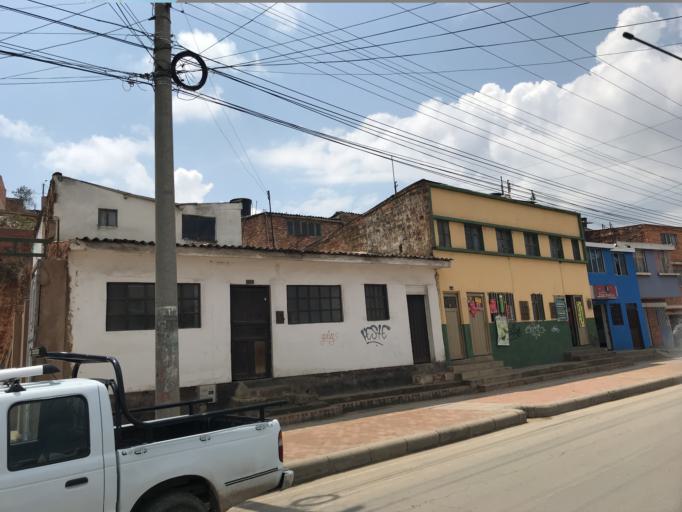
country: CO
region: Boyaca
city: Tunja
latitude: 5.5405
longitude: -73.3682
